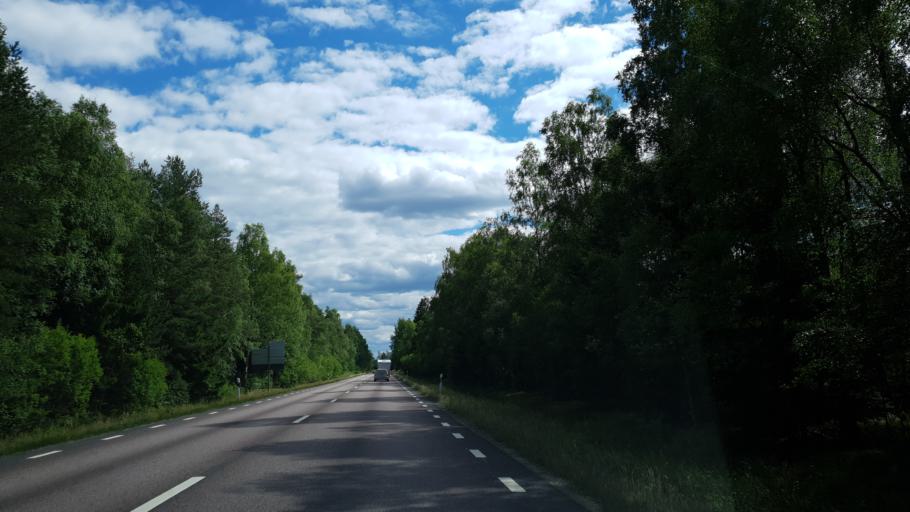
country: SE
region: Kronoberg
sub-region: Lessebo Kommun
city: Lessebo
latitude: 56.8422
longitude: 15.3903
